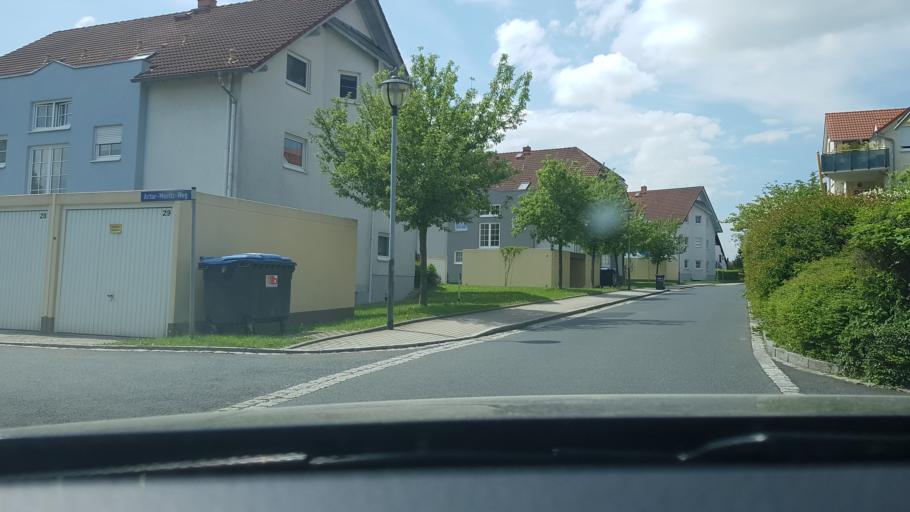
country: DE
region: Saxony
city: Freital
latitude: 51.0290
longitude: 13.6484
